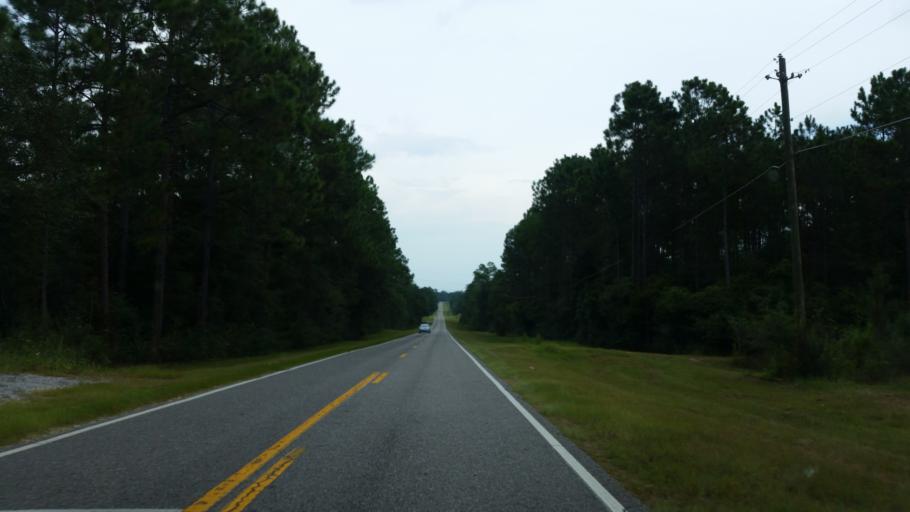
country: US
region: Florida
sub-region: Escambia County
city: Molino
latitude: 30.6803
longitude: -87.3477
